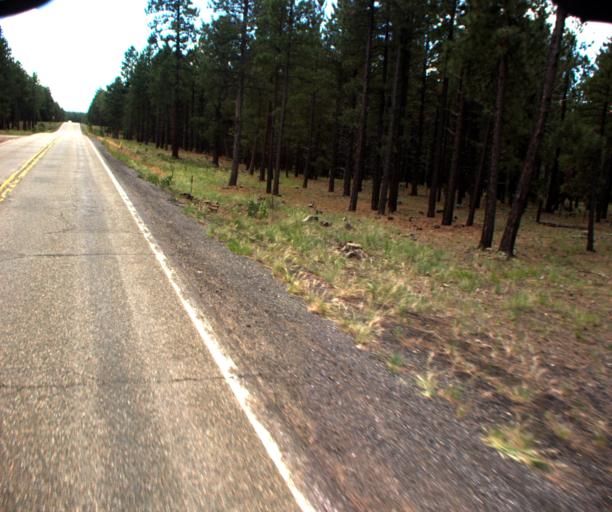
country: US
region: Arizona
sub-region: Coconino County
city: Parks
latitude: 35.3501
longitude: -111.7904
